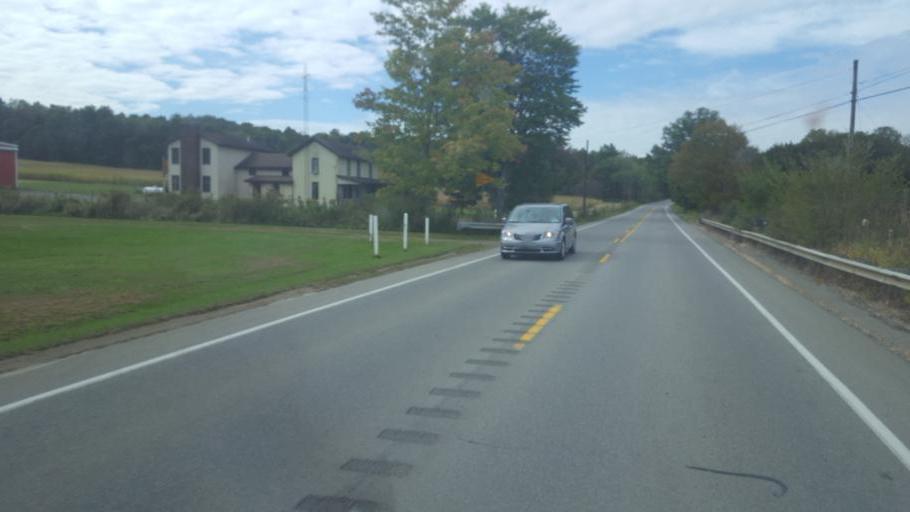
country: US
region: Pennsylvania
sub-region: Mercer County
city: Greenville
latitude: 41.4192
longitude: -80.3044
